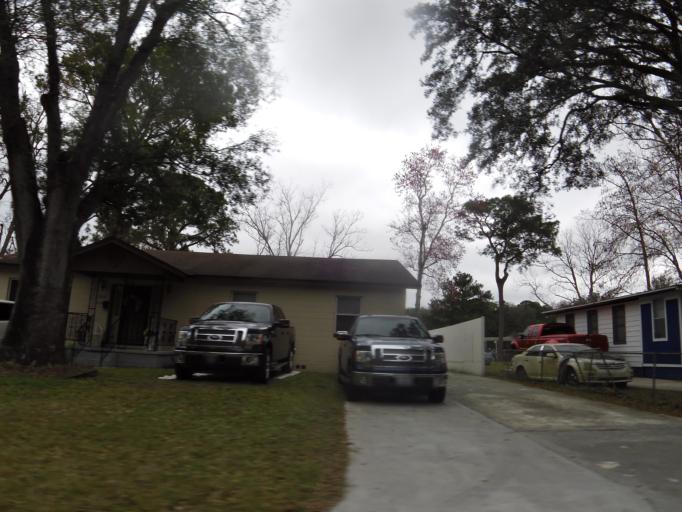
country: US
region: Florida
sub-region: Duval County
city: Jacksonville
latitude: 30.3731
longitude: -81.7058
